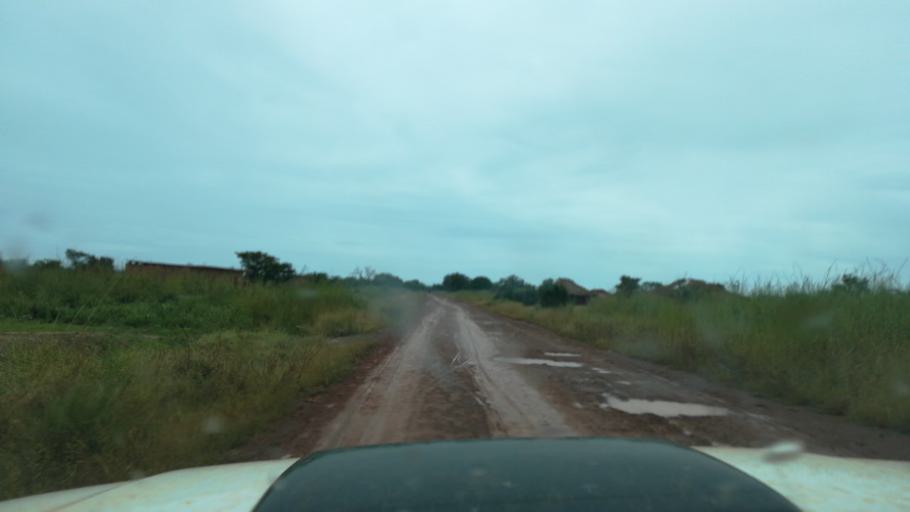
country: ZM
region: Luapula
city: Mwense
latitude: -10.1556
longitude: 28.1231
